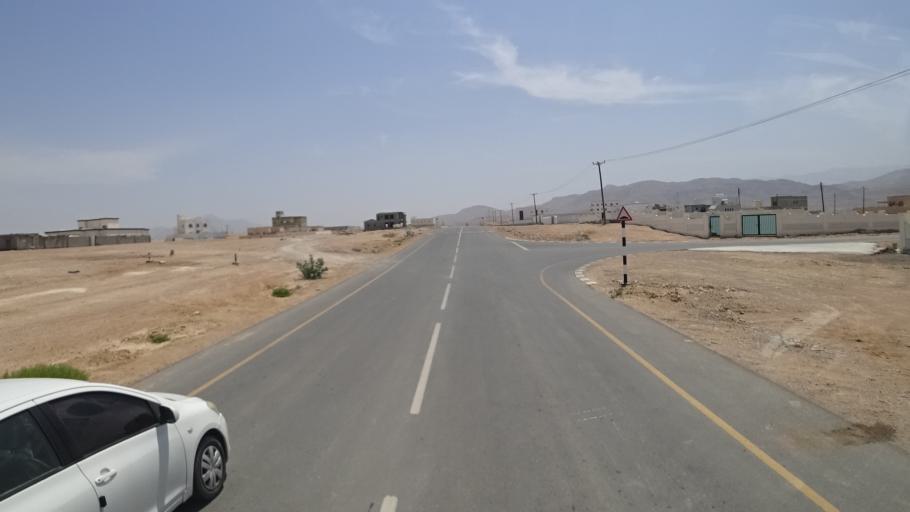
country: OM
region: Ash Sharqiyah
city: Sur
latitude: 22.5964
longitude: 59.4608
